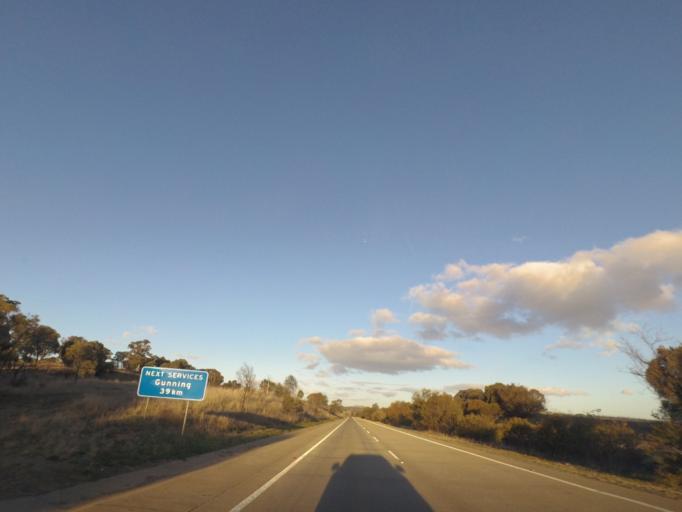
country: AU
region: New South Wales
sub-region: Yass Valley
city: Yass
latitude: -34.8076
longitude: 148.8895
